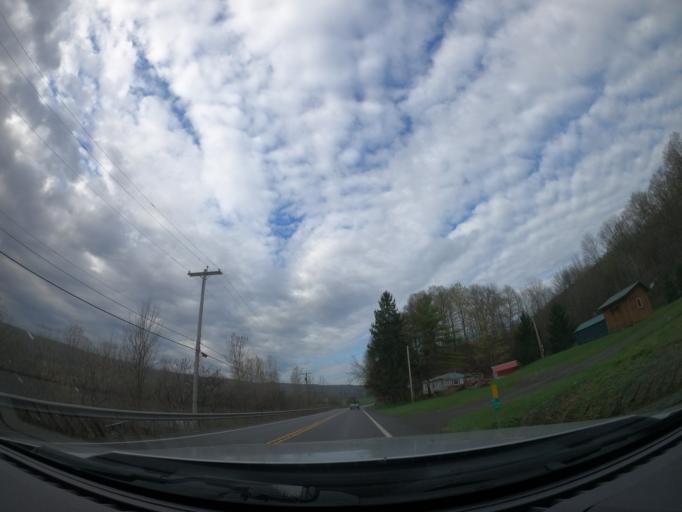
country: US
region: New York
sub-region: Cortland County
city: McGraw
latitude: 42.6859
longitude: -76.0541
